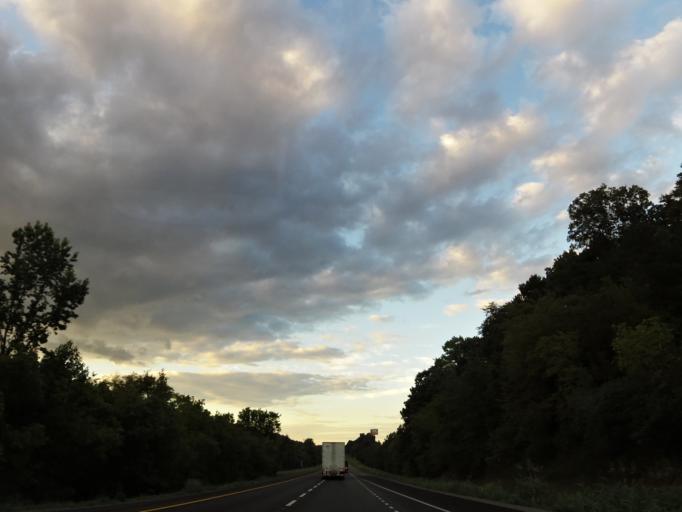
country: US
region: Tennessee
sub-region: Bradley County
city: Hopewell
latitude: 35.2938
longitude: -84.8126
